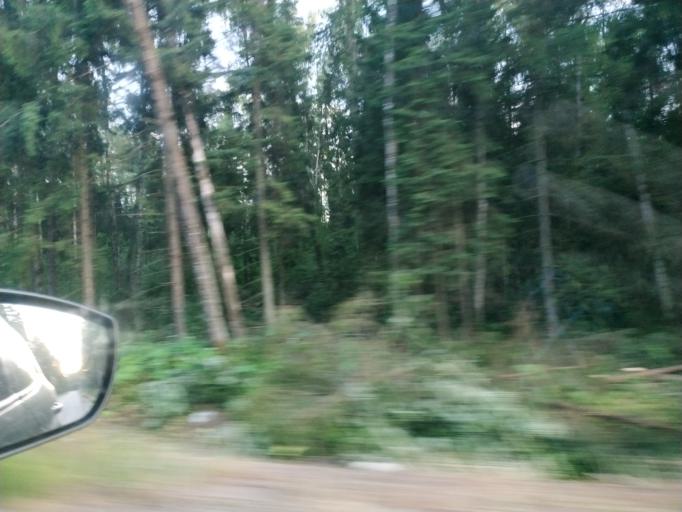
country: RU
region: Moskovskaya
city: Krasnoarmeysk
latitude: 56.0714
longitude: 38.2530
